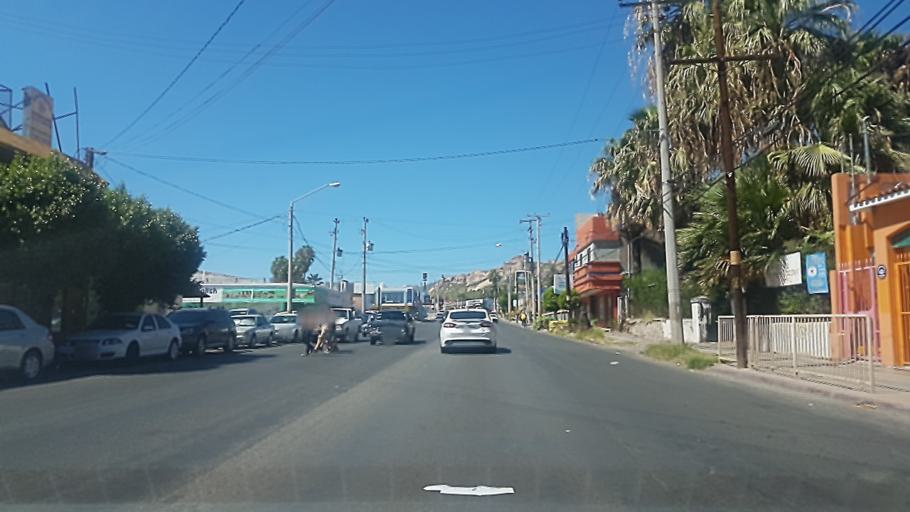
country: MX
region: Sonora
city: Heroica Guaymas
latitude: 27.9241
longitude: -110.9038
